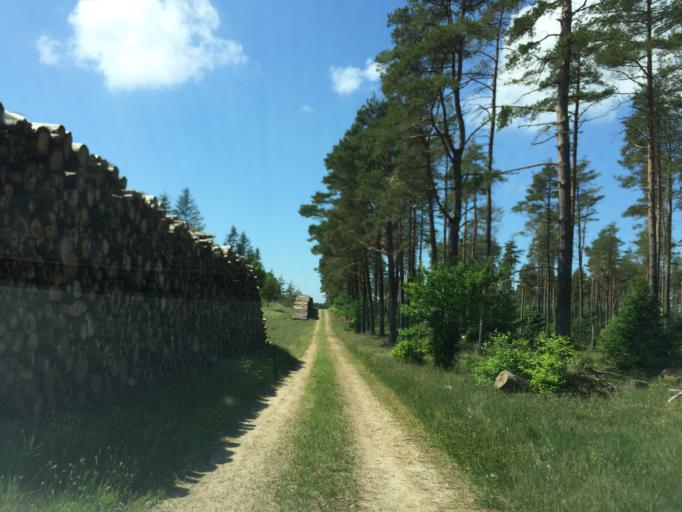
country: DK
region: Central Jutland
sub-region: Holstebro Kommune
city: Ulfborg
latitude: 56.2141
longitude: 8.4426
